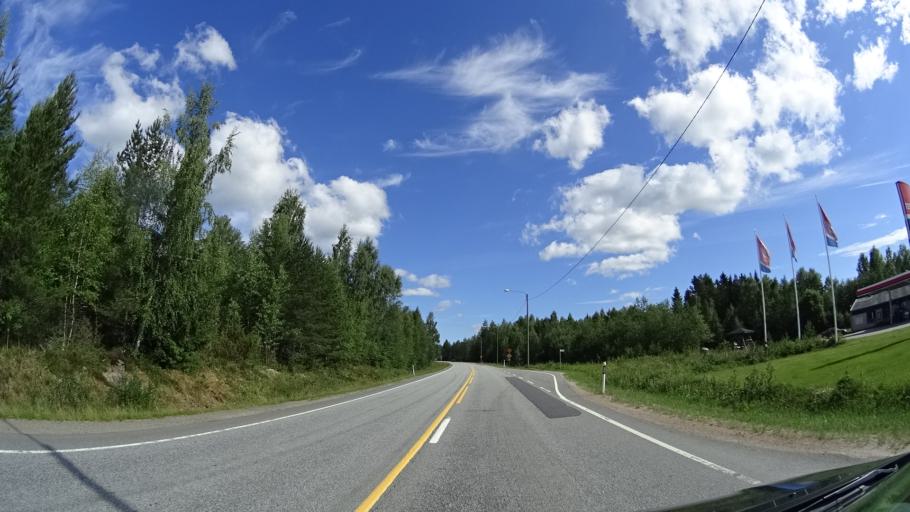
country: FI
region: Pirkanmaa
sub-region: Luoteis-Pirkanmaa
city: Kihnioe
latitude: 62.1758
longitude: 23.1700
